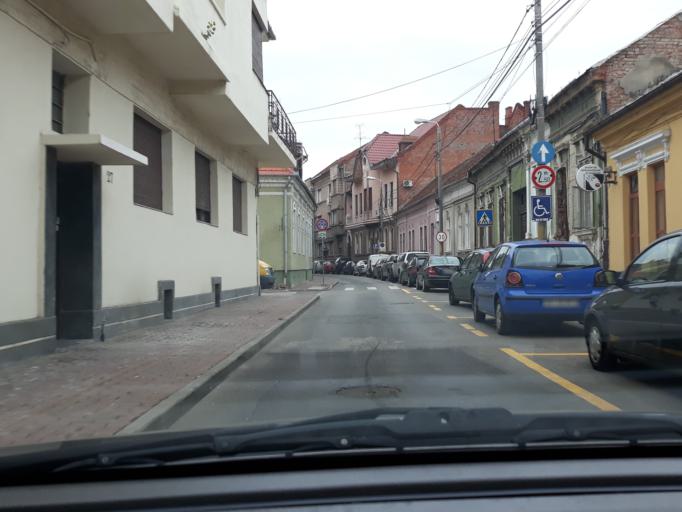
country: RO
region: Bihor
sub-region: Comuna Biharea
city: Oradea
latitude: 47.0586
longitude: 21.9278
